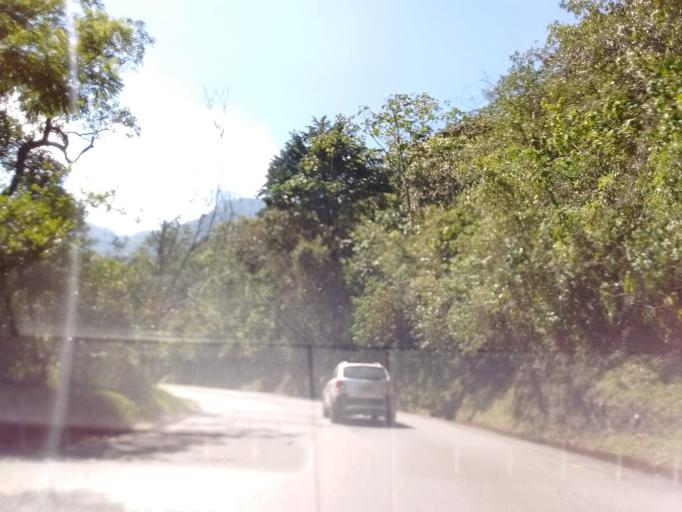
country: CO
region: Antioquia
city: Medellin
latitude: 6.2271
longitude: -75.5199
